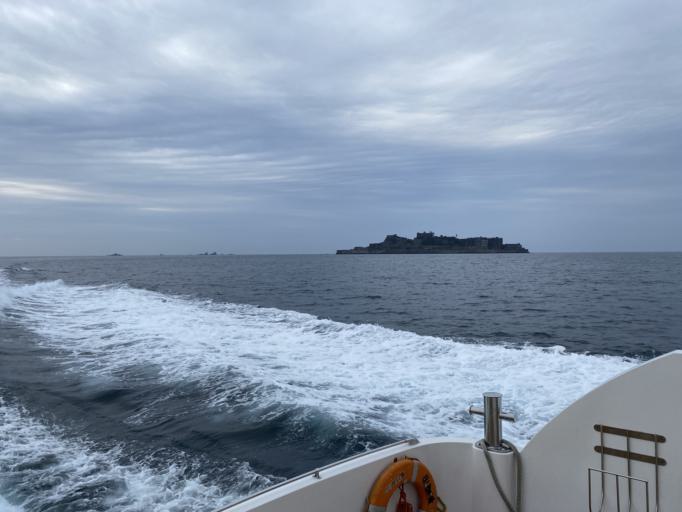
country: JP
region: Nagasaki
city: Nagasaki-shi
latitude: 32.6261
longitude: 129.7514
